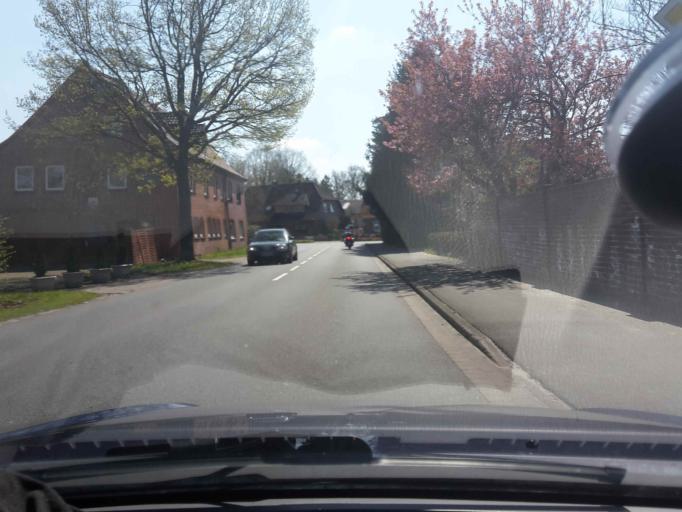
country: DE
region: Lower Saxony
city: Schneverdingen
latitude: 53.0809
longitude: 9.8562
